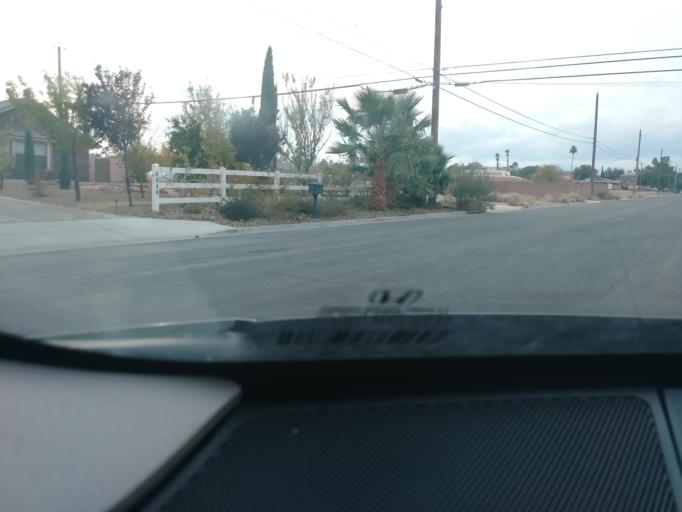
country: US
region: Nevada
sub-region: Clark County
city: Spring Valley
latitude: 36.1405
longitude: -115.2460
